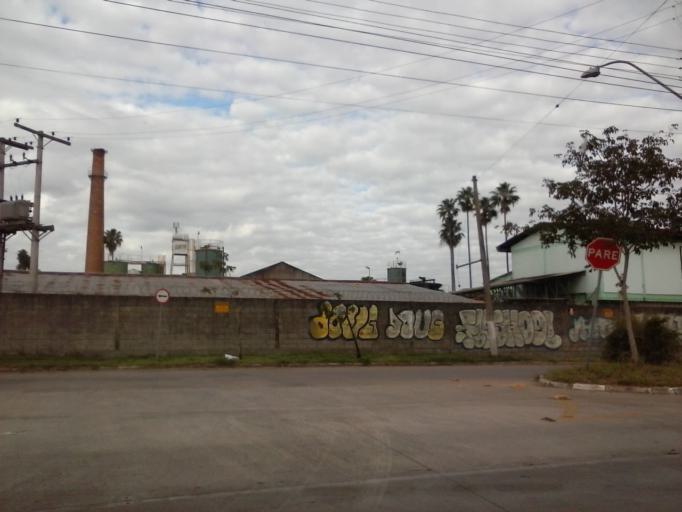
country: BR
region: Rio Grande do Sul
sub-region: Porto Alegre
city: Porto Alegre
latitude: -29.9963
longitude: -51.2056
